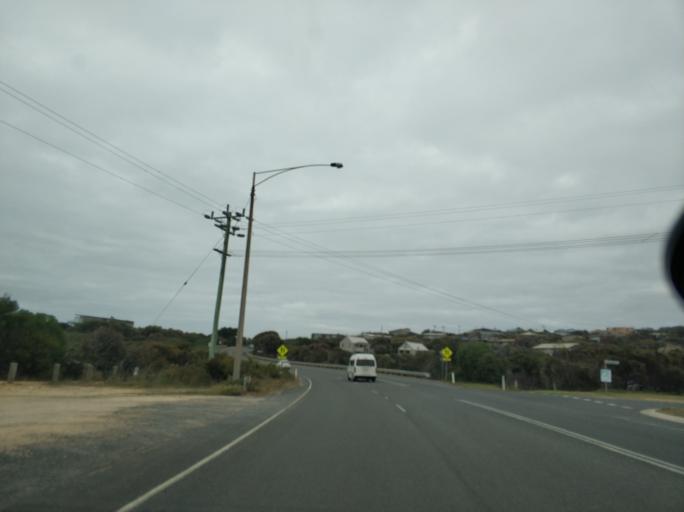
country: AU
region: Victoria
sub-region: Surf Coast
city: Anglesea
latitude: -38.4658
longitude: 144.0919
